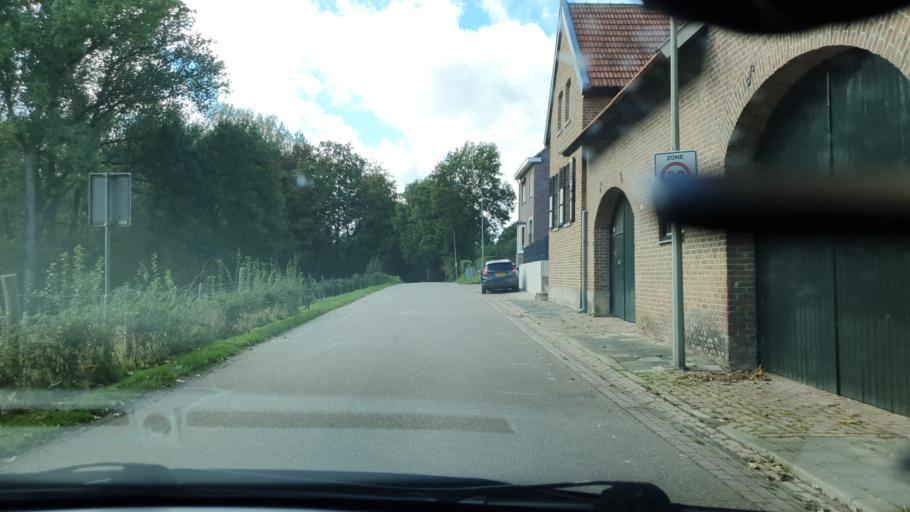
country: NL
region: Limburg
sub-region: Gemeente Nuth
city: Nuth
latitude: 50.9167
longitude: 5.8674
